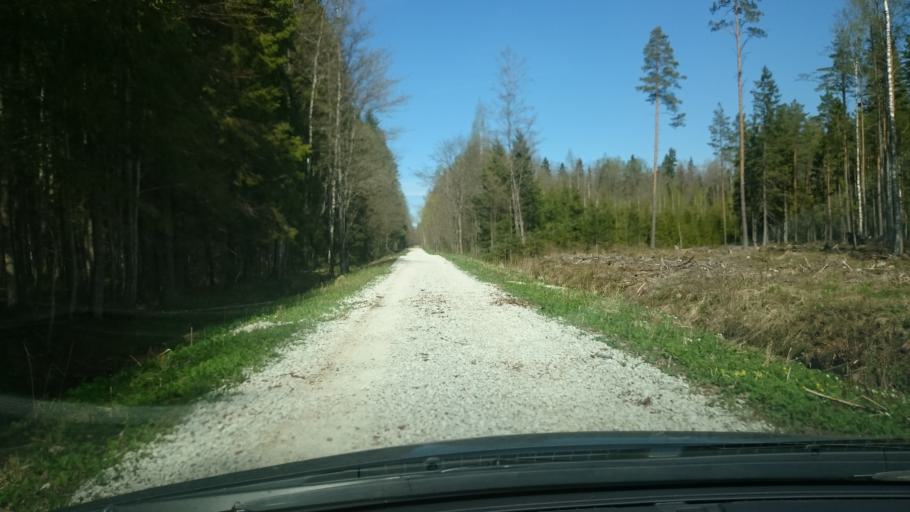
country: EE
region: Ida-Virumaa
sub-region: Sillamaee linn
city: Sillamae
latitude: 59.1675
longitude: 27.7988
